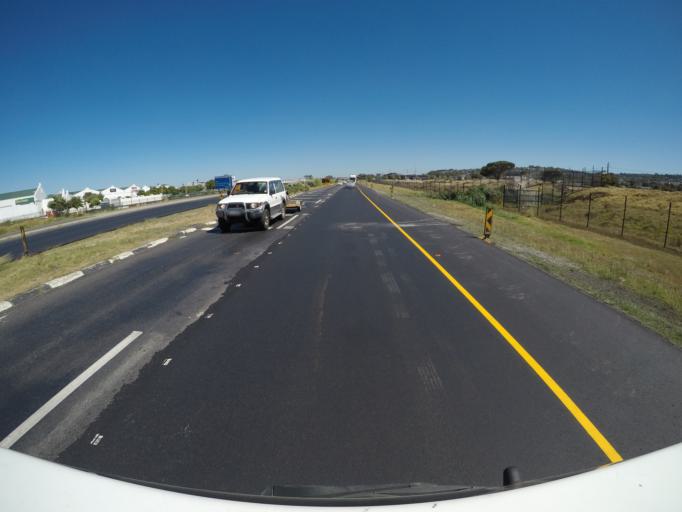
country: ZA
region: Western Cape
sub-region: Cape Winelands District Municipality
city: Stellenbosch
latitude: -34.0826
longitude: 18.8274
